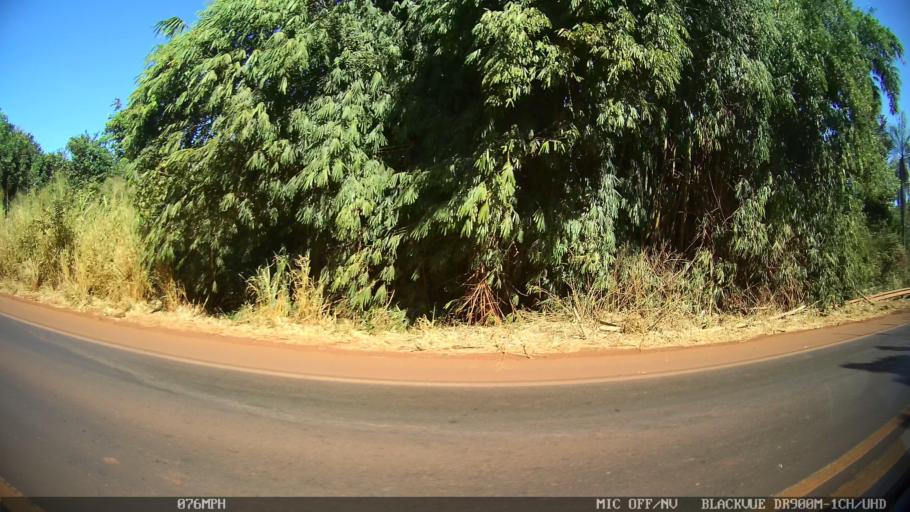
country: BR
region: Sao Paulo
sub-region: Guaira
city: Guaira
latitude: -20.4451
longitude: -48.3888
